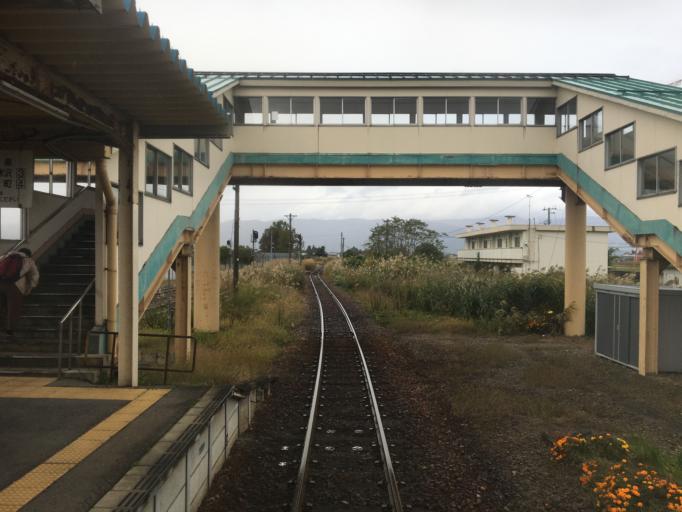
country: JP
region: Yamagata
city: Nagai
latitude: 38.0571
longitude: 140.0440
